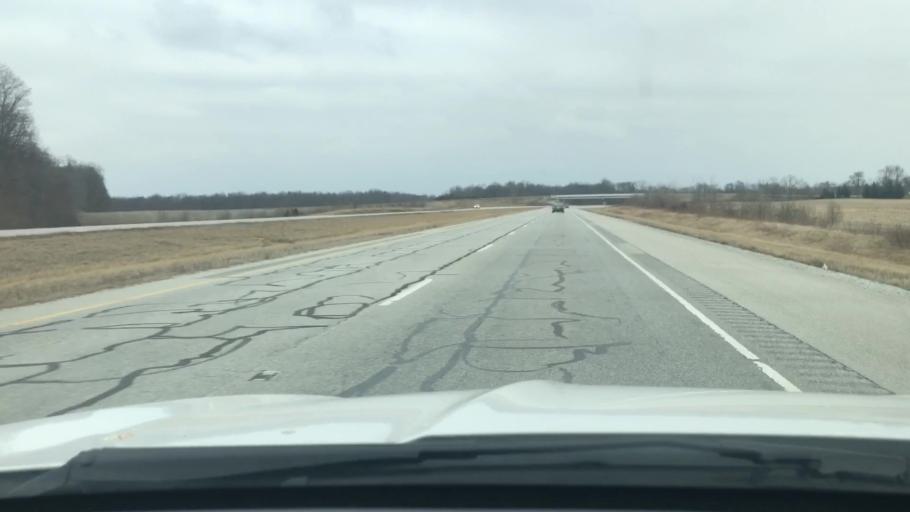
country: US
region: Indiana
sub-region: Carroll County
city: Delphi
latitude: 40.6402
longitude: -86.5816
